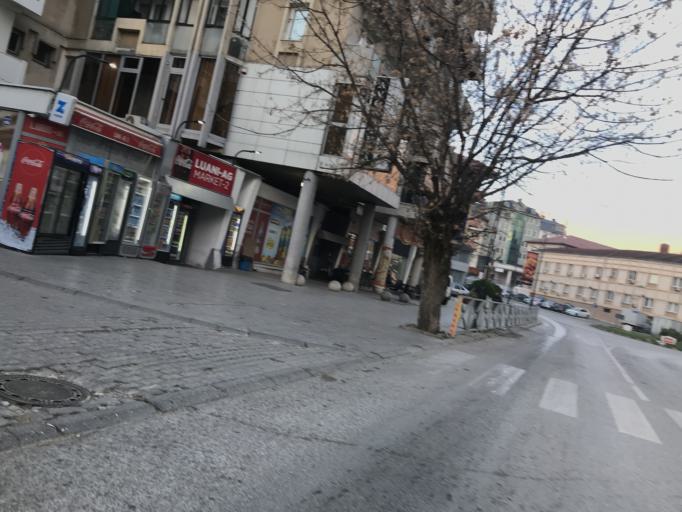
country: XK
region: Pec
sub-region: Komuna e Pejes
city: Peje
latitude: 42.6621
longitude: 20.2977
